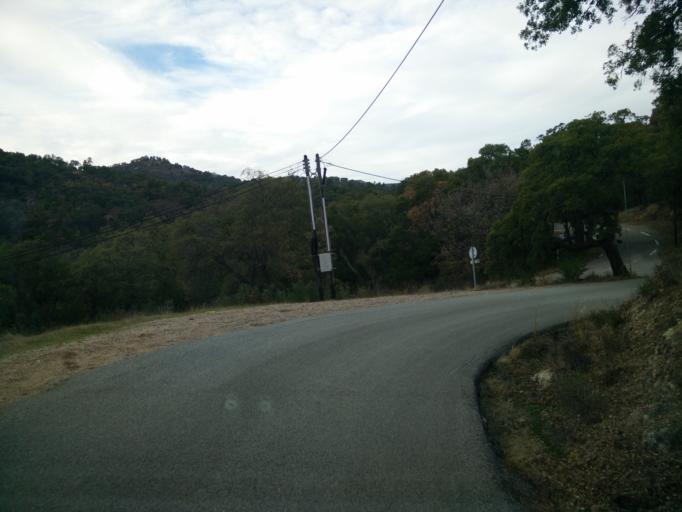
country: FR
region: Provence-Alpes-Cote d'Azur
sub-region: Departement du Var
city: Le Plan-de-la-Tour
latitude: 43.3699
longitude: 6.5989
